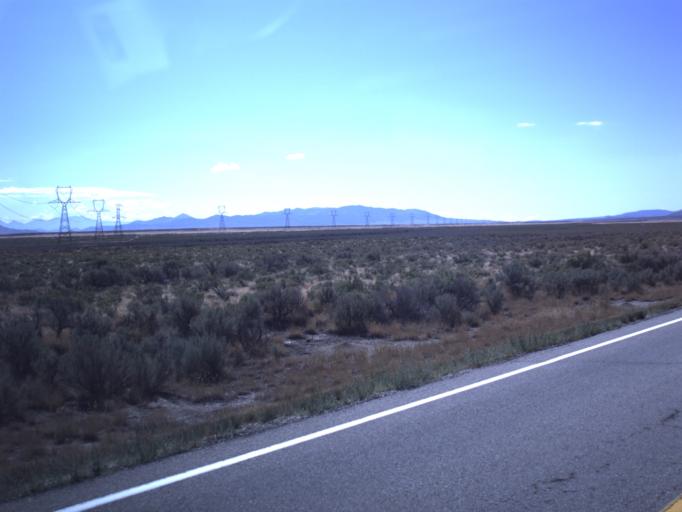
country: US
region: Utah
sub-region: Tooele County
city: Tooele
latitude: 40.2559
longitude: -112.3986
